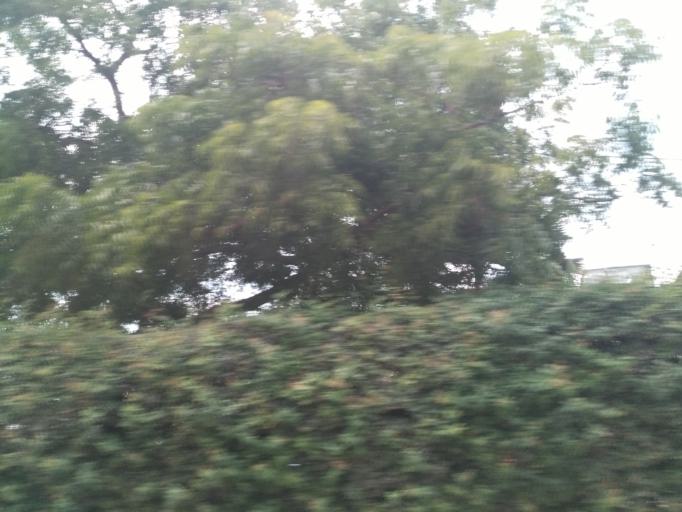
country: TZ
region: Dar es Salaam
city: Magomeni
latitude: -6.7669
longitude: 39.2452
